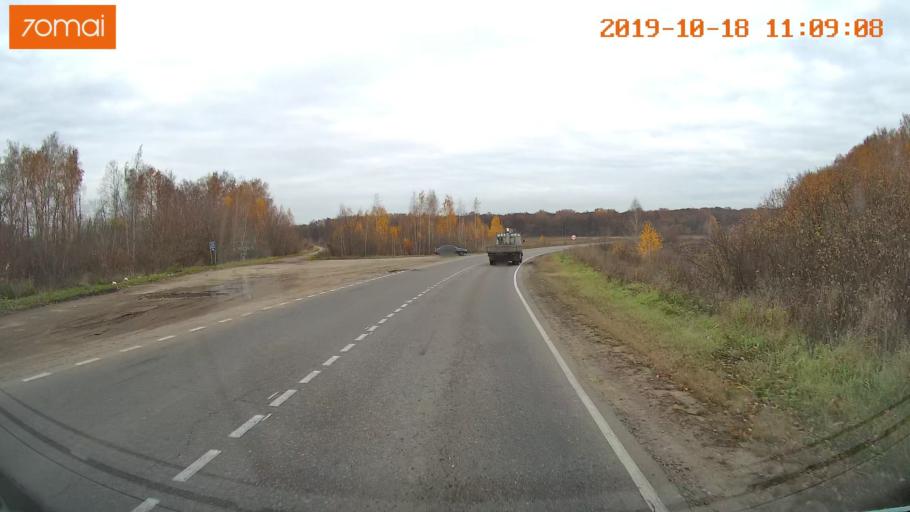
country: RU
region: Tula
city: Kimovsk
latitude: 53.9486
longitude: 38.5326
